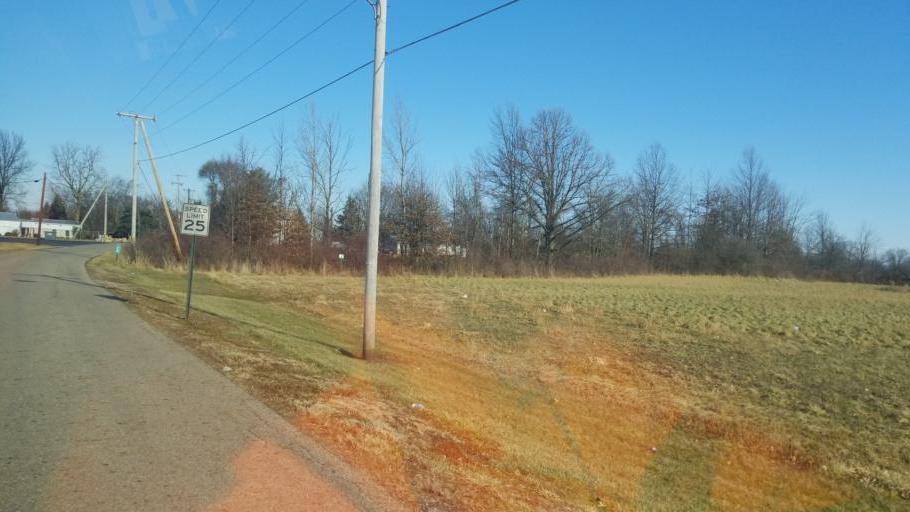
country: US
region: Ohio
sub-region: Crawford County
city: Crestline
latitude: 40.7754
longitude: -82.7479
